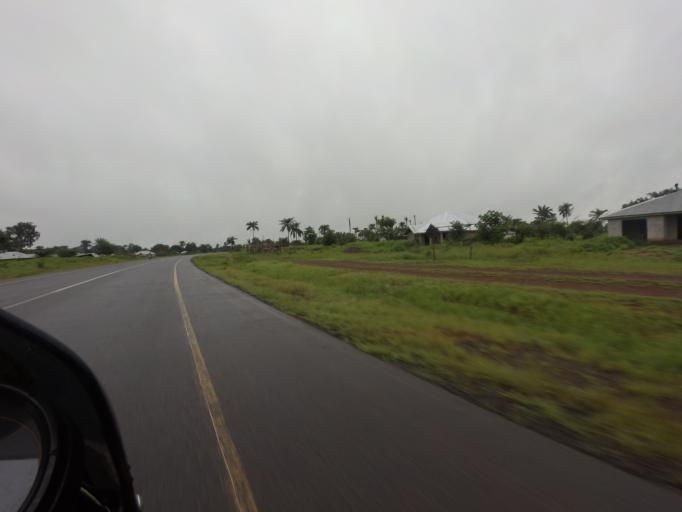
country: SL
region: Northern Province
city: Kambia
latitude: 9.0935
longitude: -12.9093
